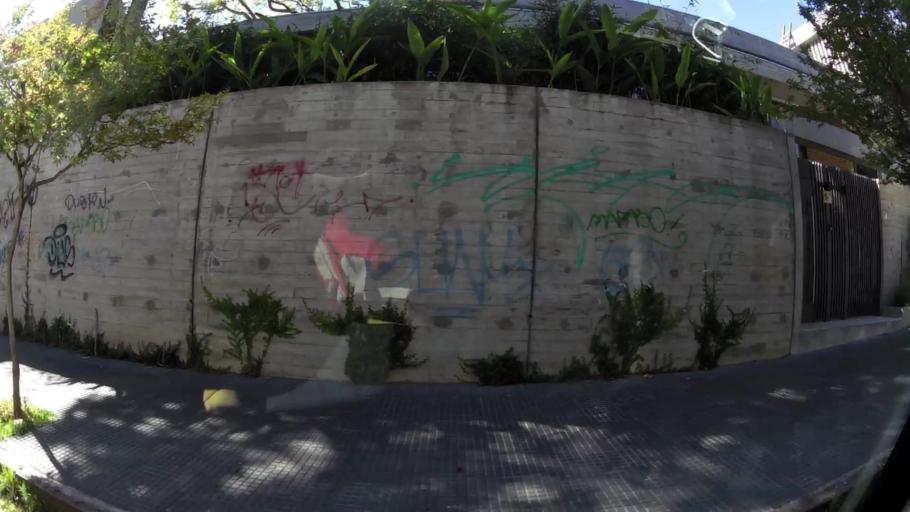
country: AR
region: Buenos Aires
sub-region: Partido de Vicente Lopez
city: Olivos
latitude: -34.5247
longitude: -58.4780
